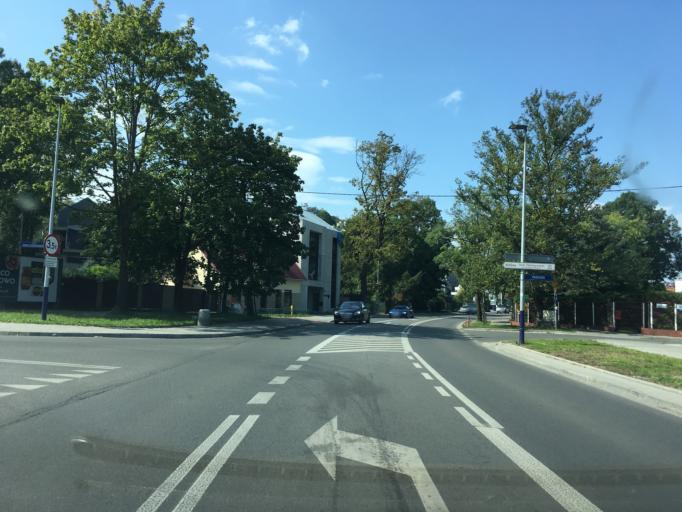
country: PL
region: Lesser Poland Voivodeship
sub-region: Krakow
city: Krakow
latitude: 50.0564
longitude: 19.9041
